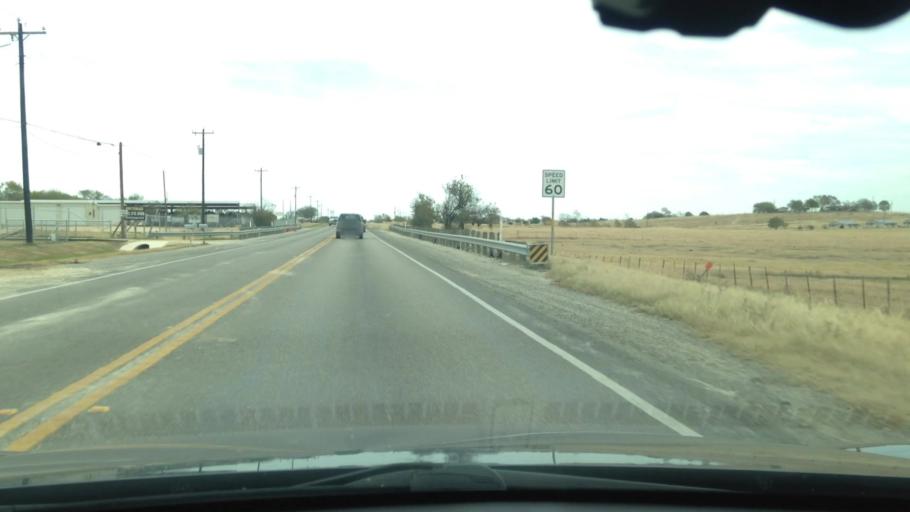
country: US
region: Texas
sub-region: Caldwell County
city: Martindale
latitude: 29.9113
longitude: -97.8561
